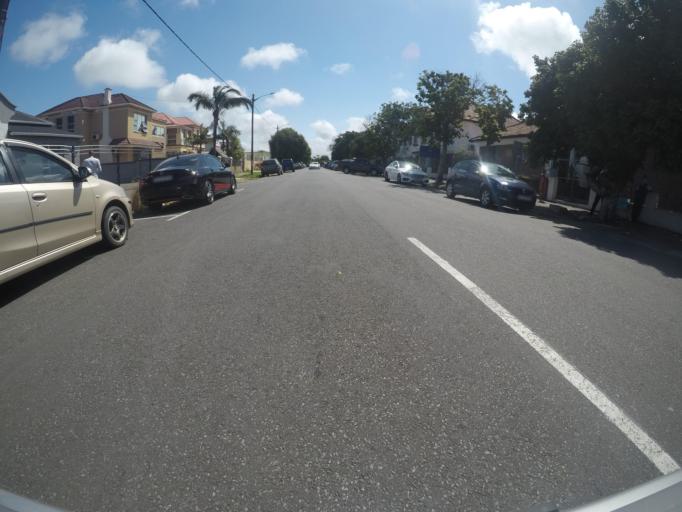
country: ZA
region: Eastern Cape
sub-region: Buffalo City Metropolitan Municipality
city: East London
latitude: -33.0029
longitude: 27.8994
